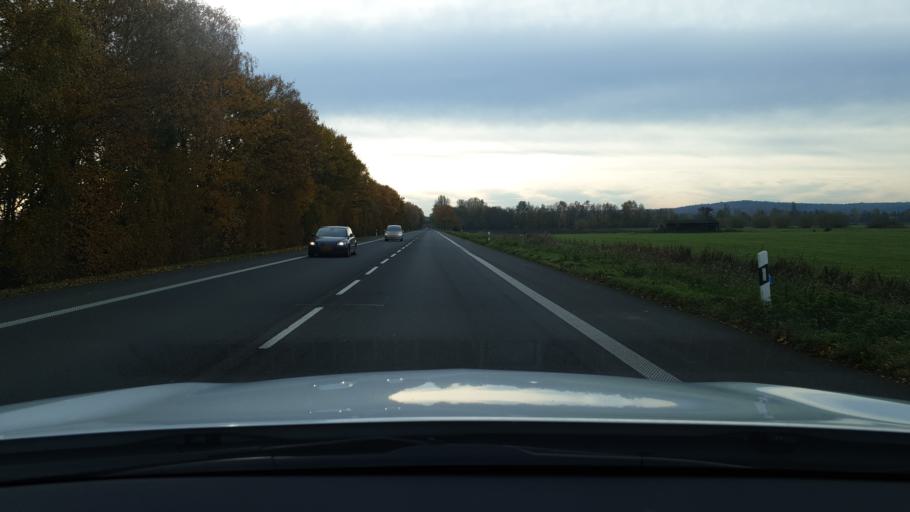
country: DE
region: North Rhine-Westphalia
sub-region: Regierungsbezirk Dusseldorf
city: Kranenburg
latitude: 51.7964
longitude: 6.0243
